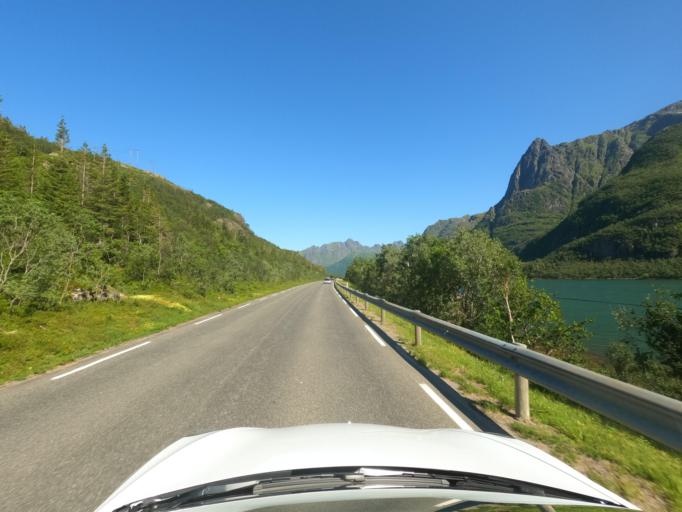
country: NO
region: Nordland
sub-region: Hadsel
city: Melbu
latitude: 68.3739
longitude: 14.7829
